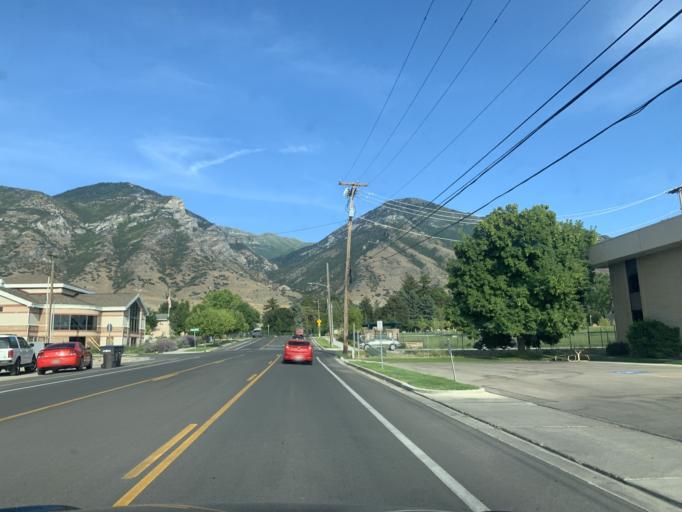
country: US
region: Utah
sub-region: Utah County
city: Provo
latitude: 40.2256
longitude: -111.6489
